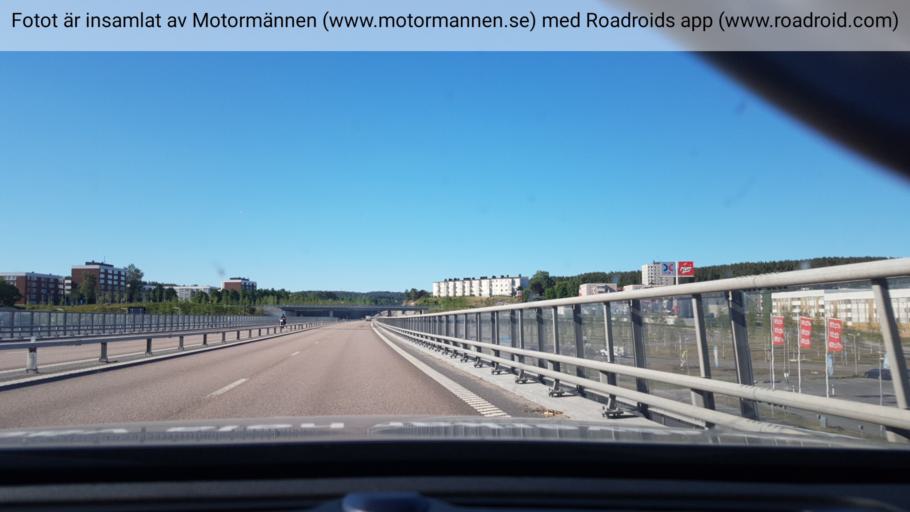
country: SE
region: Vaesternorrland
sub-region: Sundsvalls Kommun
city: Sundsvall
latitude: 62.3952
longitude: 17.3376
